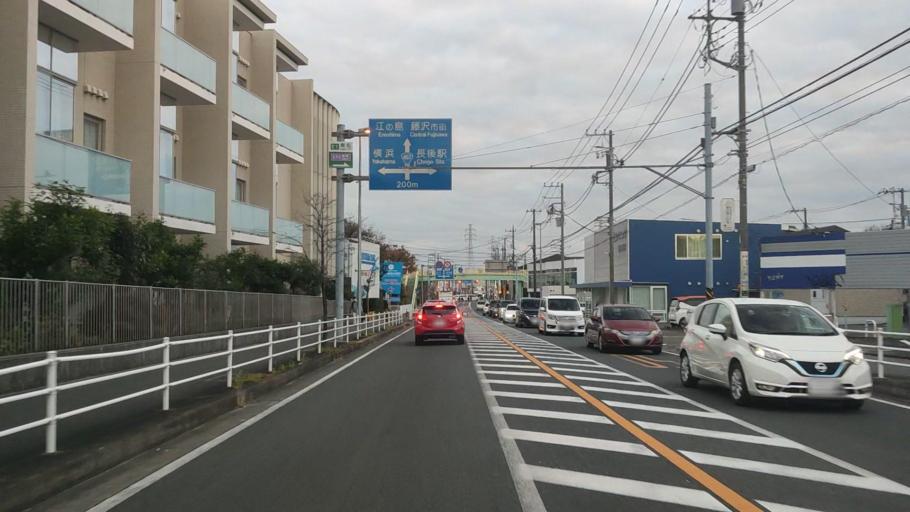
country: JP
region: Kanagawa
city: Minami-rinkan
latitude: 35.4177
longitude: 139.4694
